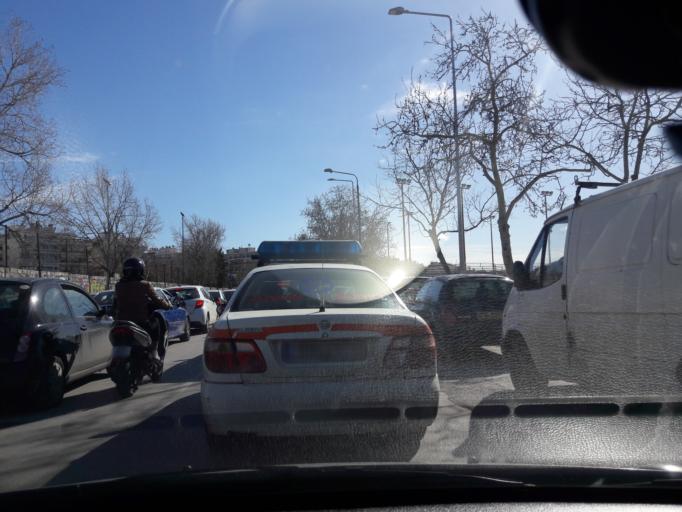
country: GR
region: Central Macedonia
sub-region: Nomos Thessalonikis
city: Kalamaria
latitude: 40.5967
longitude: 22.9504
